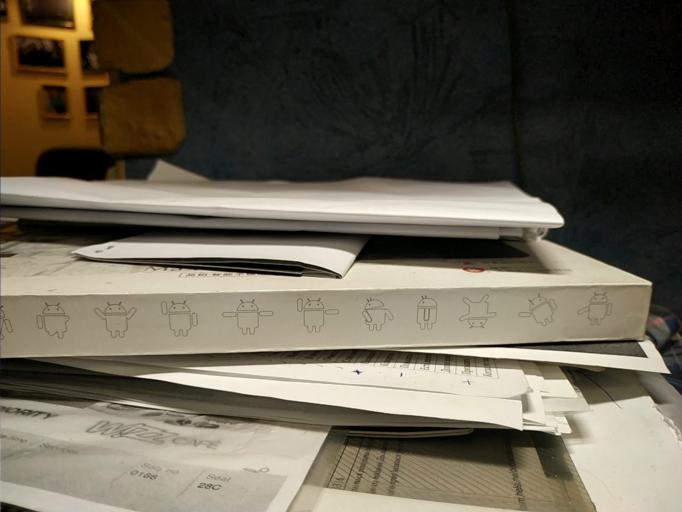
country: RU
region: Tverskaya
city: Zubtsov
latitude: 56.0859
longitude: 34.7696
